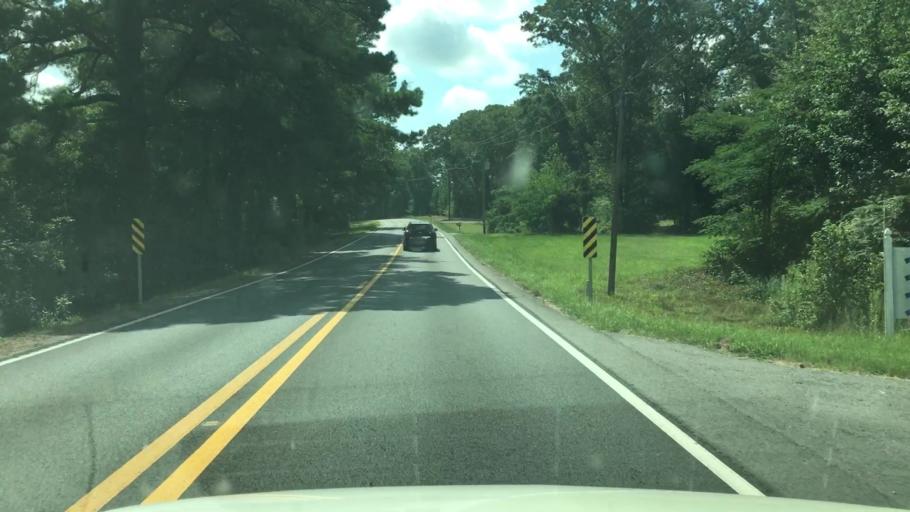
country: US
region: Arkansas
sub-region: Garland County
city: Lake Hamilton
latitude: 34.2801
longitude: -93.1593
